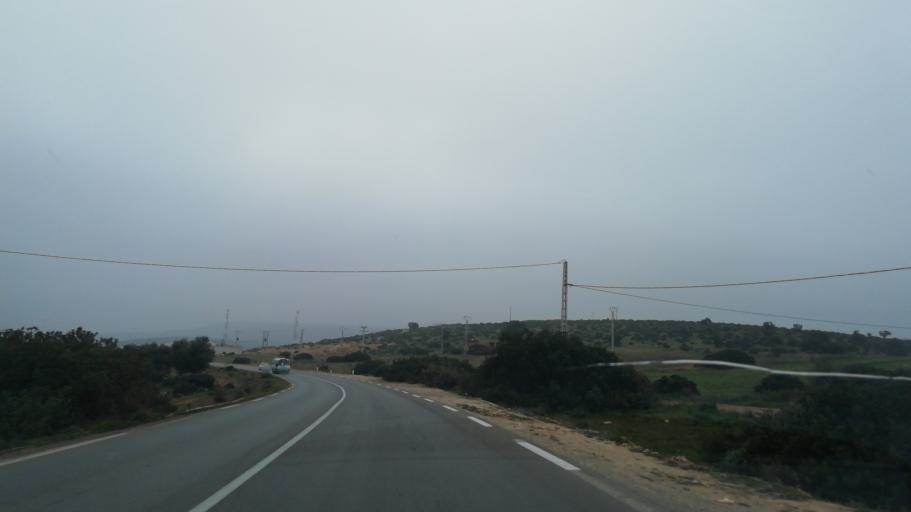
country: DZ
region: Mascara
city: Oued el Abtal
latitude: 35.2927
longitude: 0.4653
